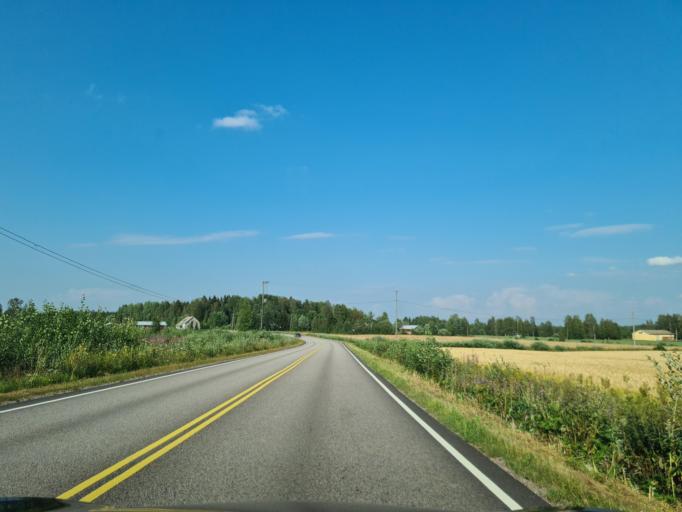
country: FI
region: Satakunta
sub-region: Pohjois-Satakunta
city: Karvia
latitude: 62.2084
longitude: 22.6023
